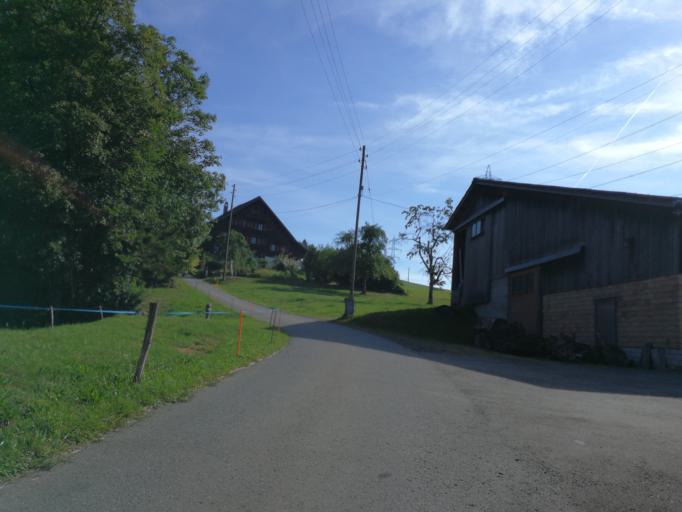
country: CH
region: Saint Gallen
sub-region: Wahlkreis See-Gaster
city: Gommiswald
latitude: 47.2463
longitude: 9.0175
